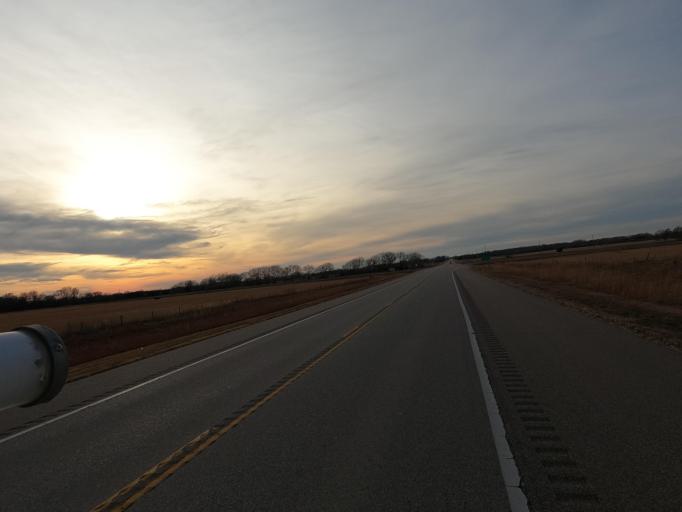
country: US
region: Kansas
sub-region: Rice County
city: Sterling
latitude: 37.9846
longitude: -98.3228
